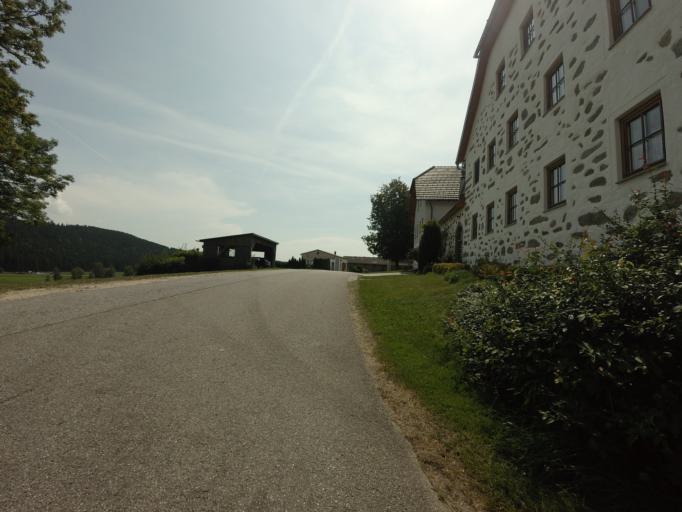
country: AT
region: Upper Austria
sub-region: Politischer Bezirk Urfahr-Umgebung
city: Schenkenfelden
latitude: 48.5223
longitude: 14.3606
